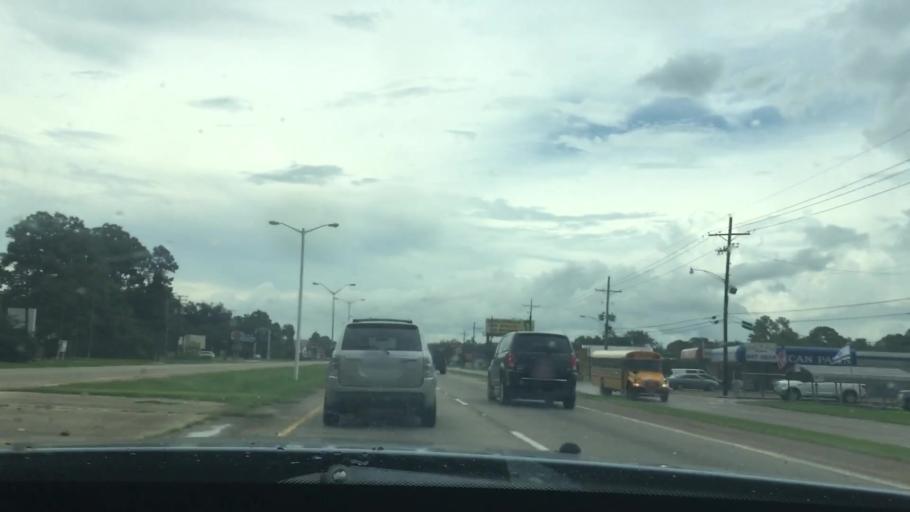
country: US
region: Louisiana
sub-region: East Baton Rouge Parish
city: Monticello
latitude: 30.4567
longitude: -91.0717
